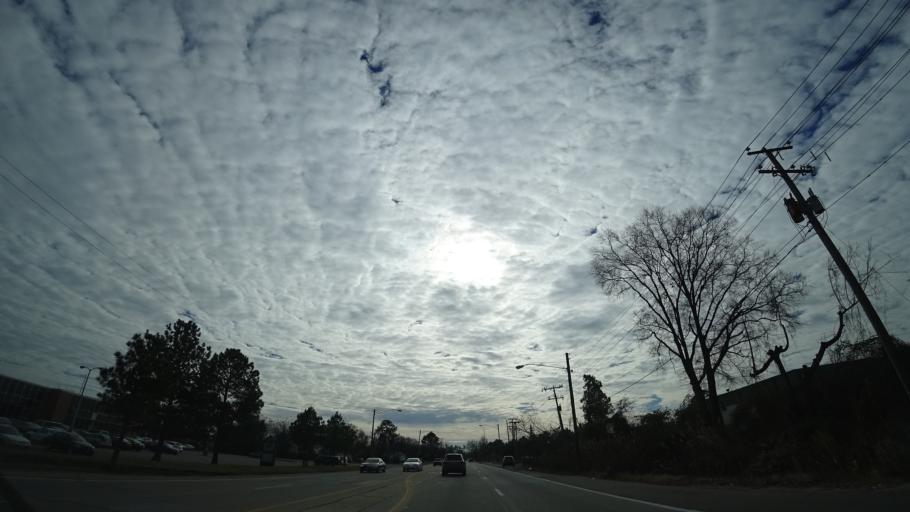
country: US
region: Virginia
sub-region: City of Hampton
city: Hampton
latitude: 37.0314
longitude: -76.3629
